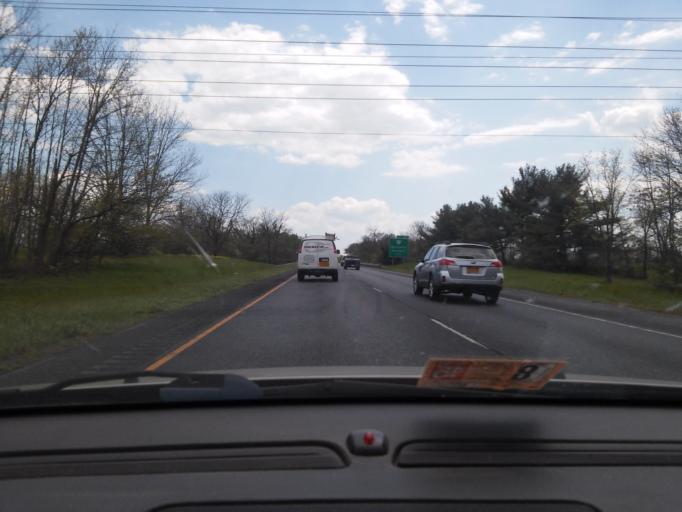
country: US
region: Virginia
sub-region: City of Winchester
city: Winchester
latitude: 39.2042
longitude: -78.1356
